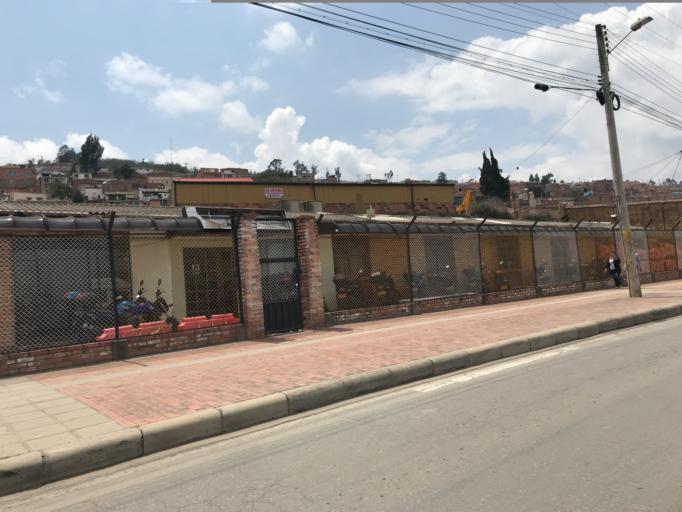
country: CO
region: Boyaca
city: Tunja
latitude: 5.5382
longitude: -73.3679
